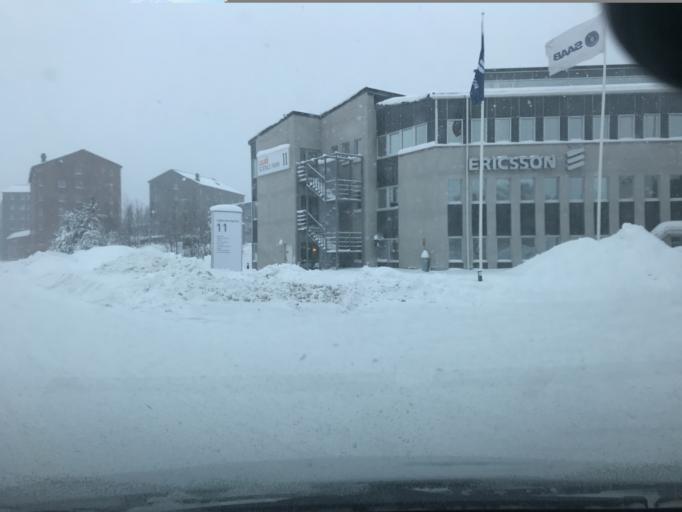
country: SE
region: Norrbotten
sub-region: Lulea Kommun
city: Lulea
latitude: 65.6205
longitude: 22.1425
